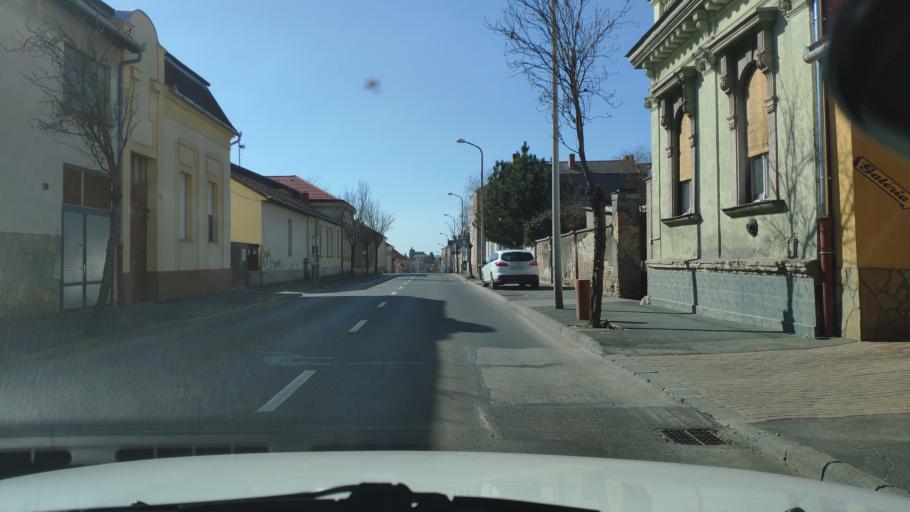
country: HU
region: Zala
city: Nagykanizsa
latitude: 46.4515
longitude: 16.9951
